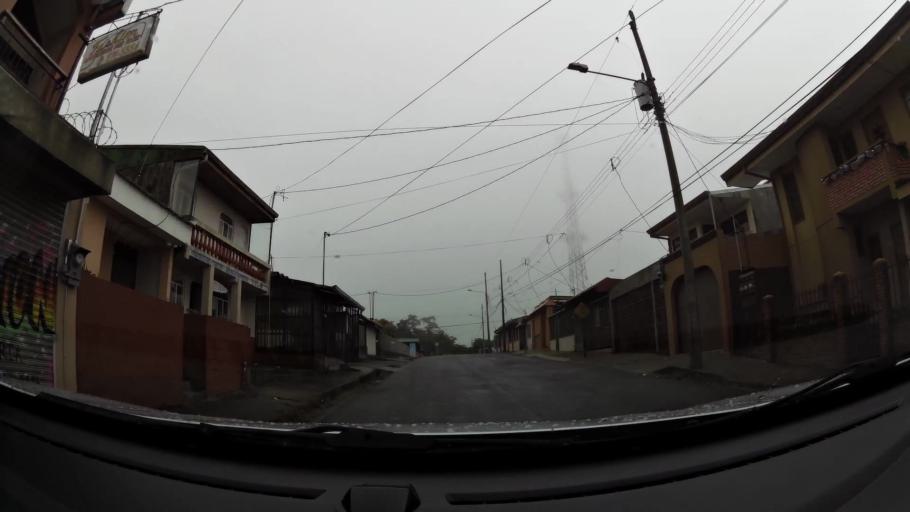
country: CR
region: Cartago
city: Paraiso
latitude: 9.8407
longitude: -83.8694
